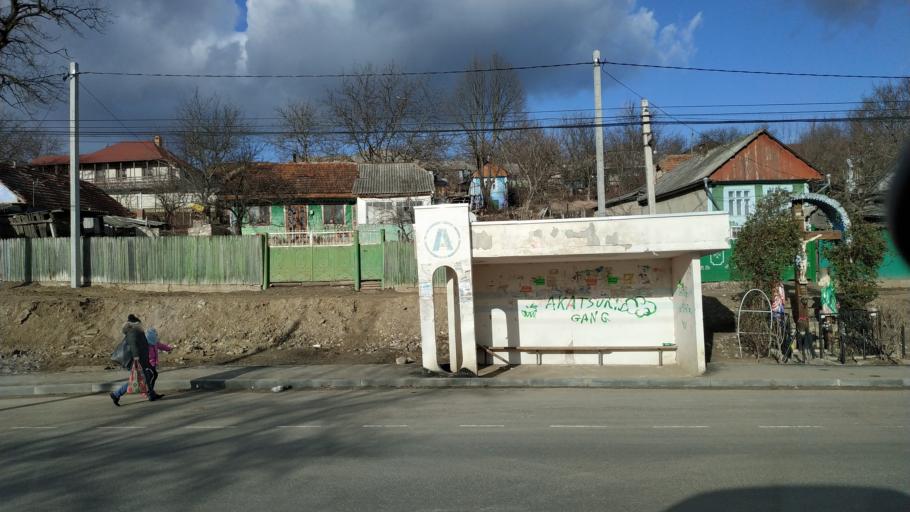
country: MD
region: Calarasi
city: Calarasi
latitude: 47.2848
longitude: 28.2005
